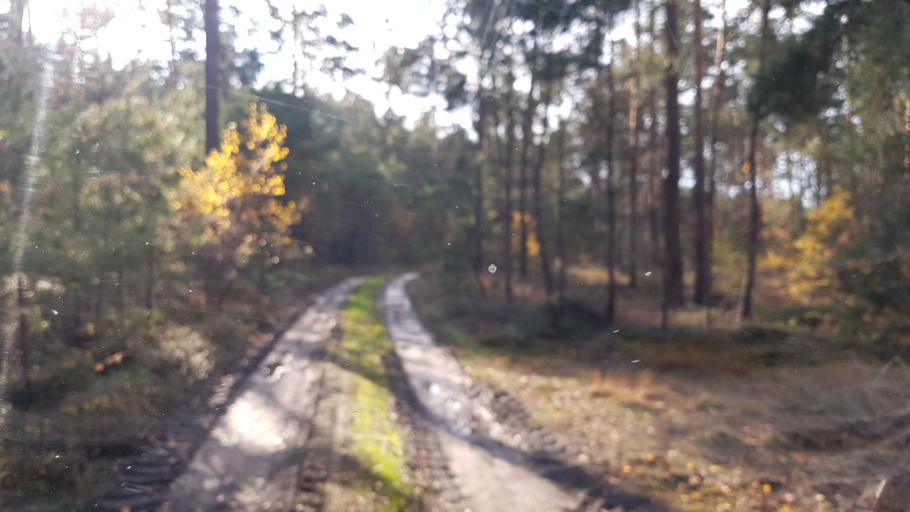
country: DE
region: Brandenburg
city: Trobitz
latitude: 51.6464
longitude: 13.4194
